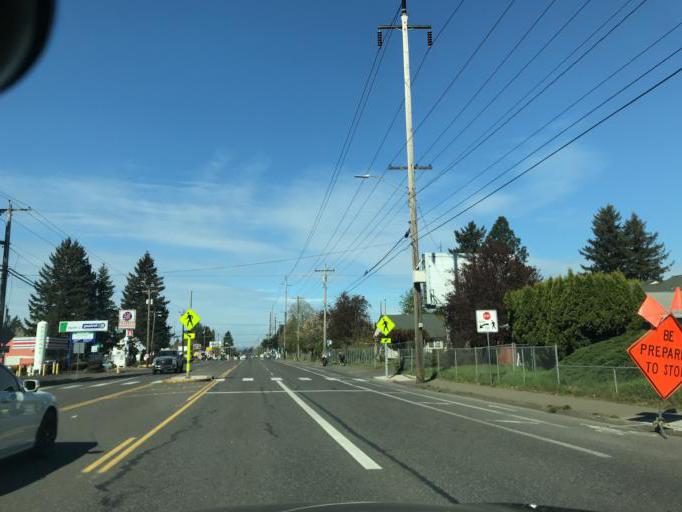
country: US
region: Oregon
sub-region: Multnomah County
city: Gresham
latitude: 45.5046
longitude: -122.4800
